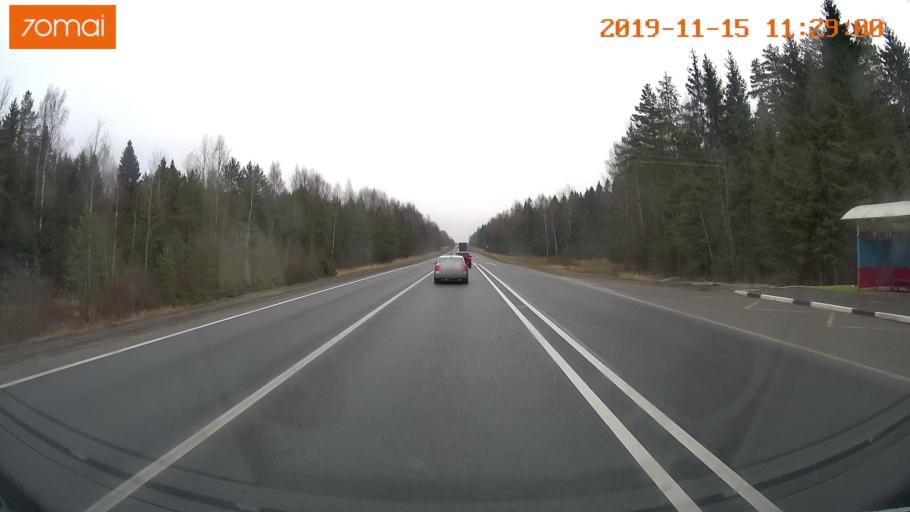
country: RU
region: Vologda
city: Molochnoye
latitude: 59.1740
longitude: 39.4998
